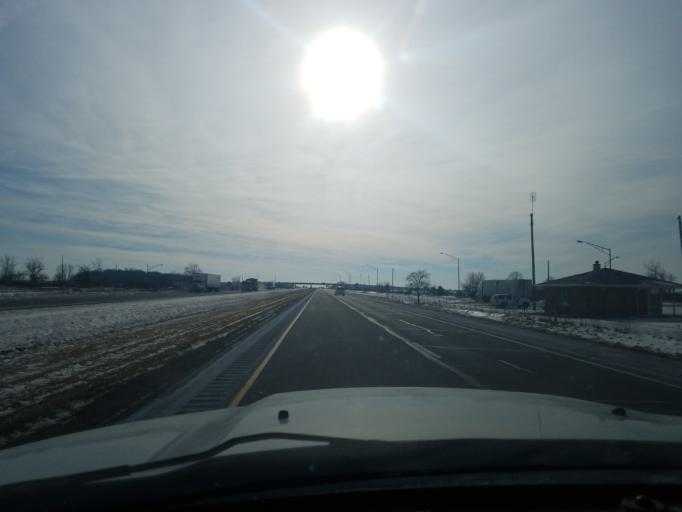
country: US
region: Indiana
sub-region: Huntington County
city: Warren
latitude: 40.7472
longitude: -85.4079
